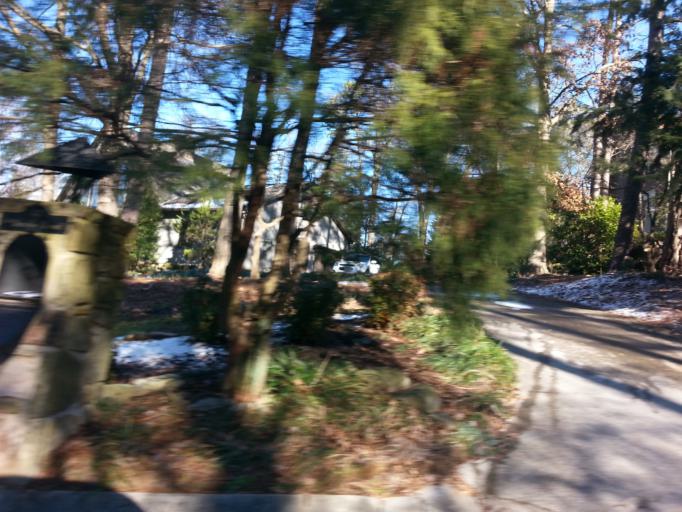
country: US
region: Tennessee
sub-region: Blount County
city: Louisville
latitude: 35.9135
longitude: -84.0144
